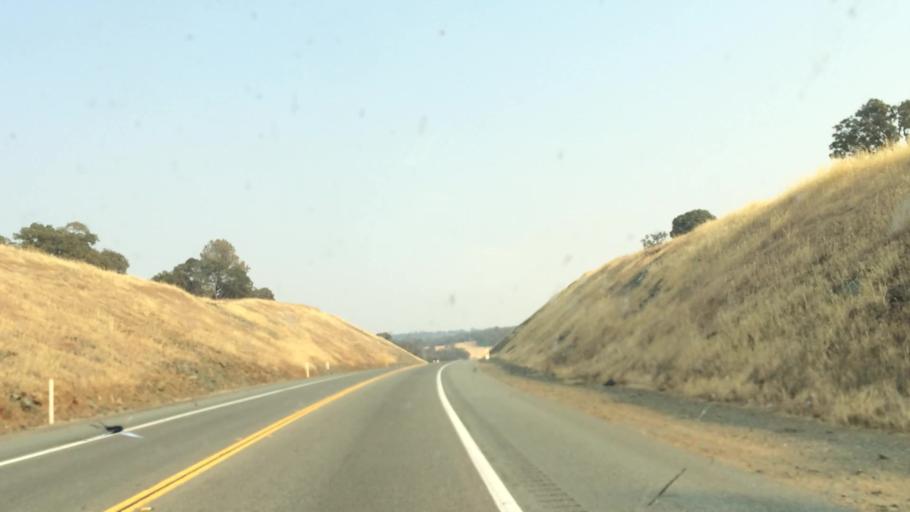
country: US
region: California
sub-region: Amador County
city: Sutter Creek
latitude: 38.4021
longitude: -120.8206
